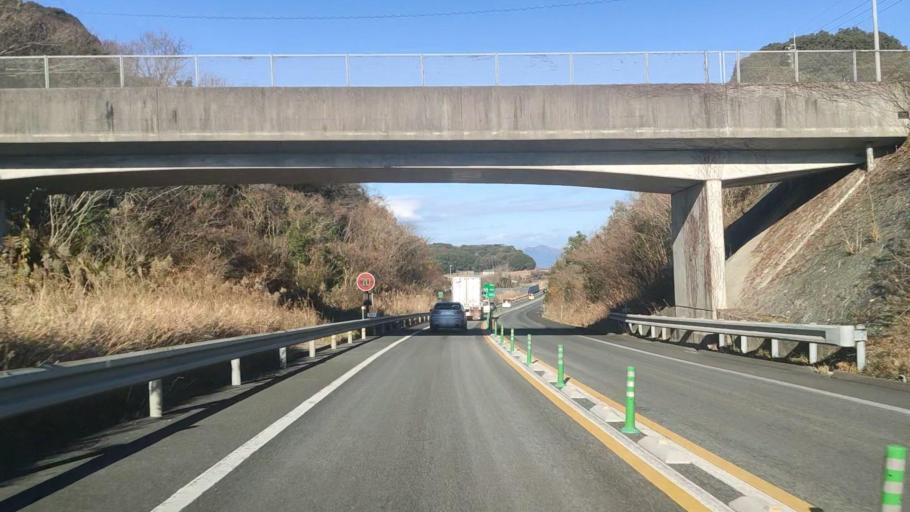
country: JP
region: Fukuoka
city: Shiida
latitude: 33.6437
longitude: 131.0412
